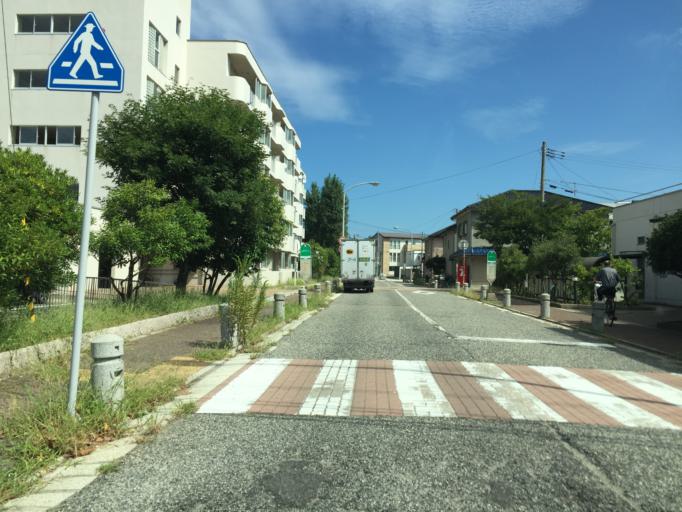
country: JP
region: Niigata
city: Niigata-shi
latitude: 37.9390
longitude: 139.0551
